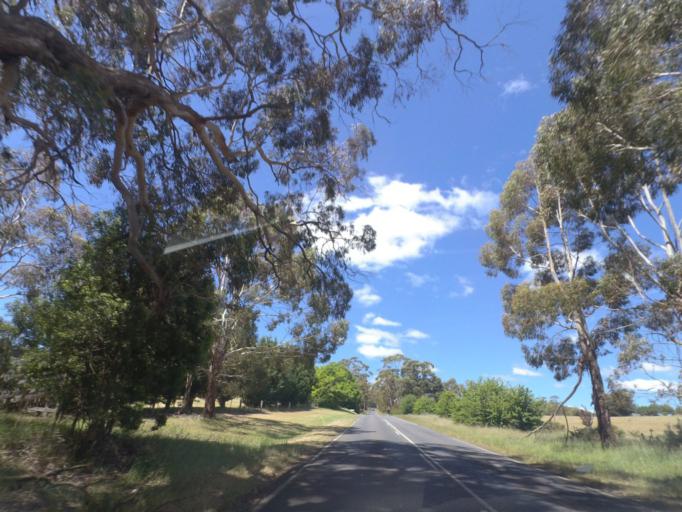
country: AU
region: Victoria
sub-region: Mount Alexander
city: Castlemaine
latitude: -37.2914
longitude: 144.2573
